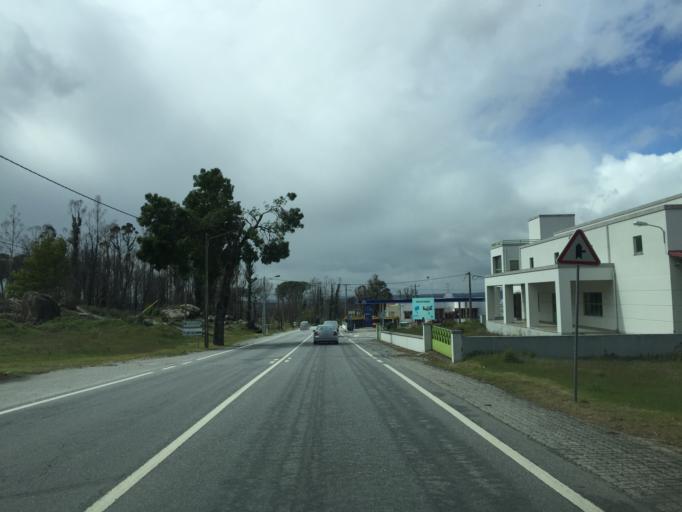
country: PT
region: Guarda
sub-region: Seia
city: Seia
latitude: 40.5084
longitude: -7.6241
